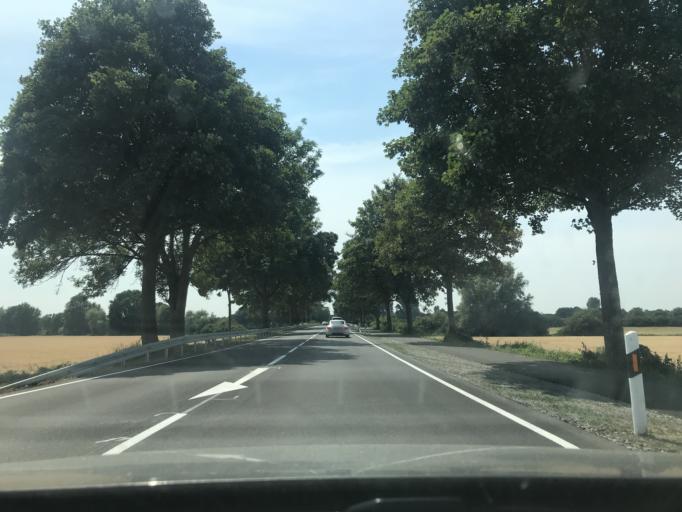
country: DE
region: North Rhine-Westphalia
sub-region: Regierungsbezirk Dusseldorf
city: Alpen
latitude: 51.6041
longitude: 6.5491
